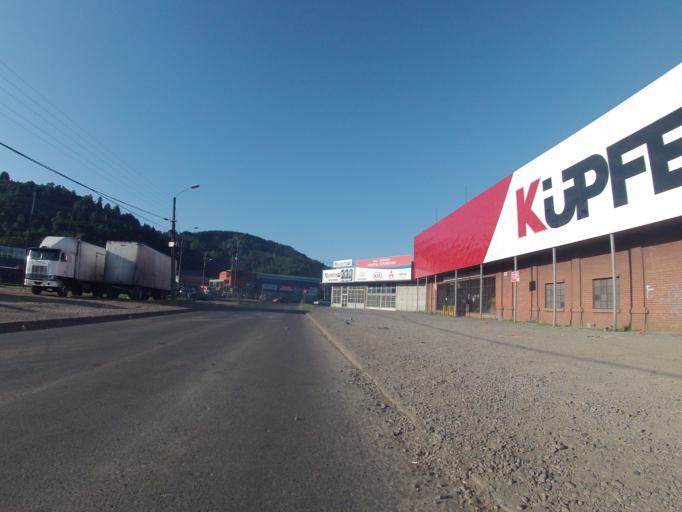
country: CL
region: Araucania
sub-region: Provincia de Cautin
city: Temuco
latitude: -38.7281
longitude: -72.5778
